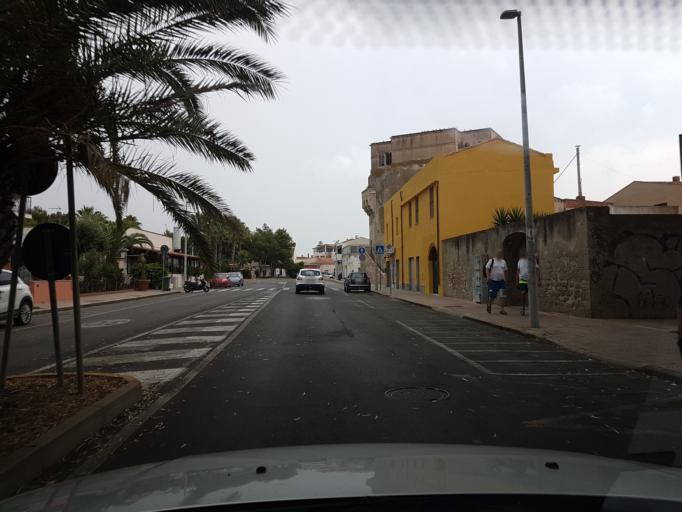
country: IT
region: Sardinia
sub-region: Provincia di Oristano
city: Cabras
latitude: 39.9071
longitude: 8.5155
